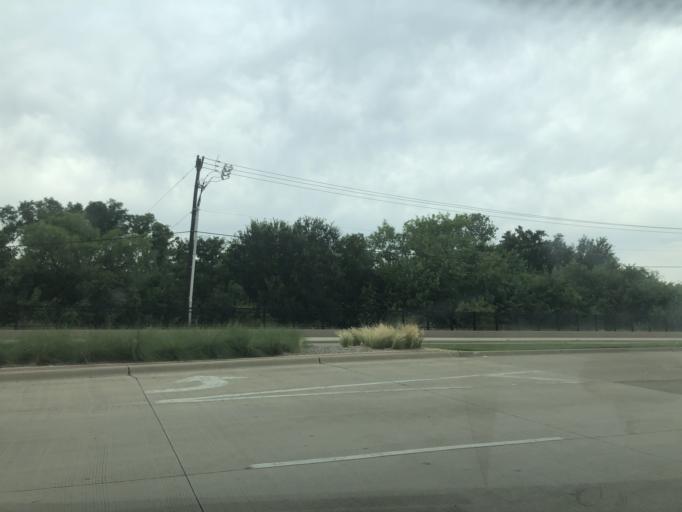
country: US
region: Texas
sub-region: Dallas County
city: Irving
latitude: 32.7830
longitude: -96.9634
